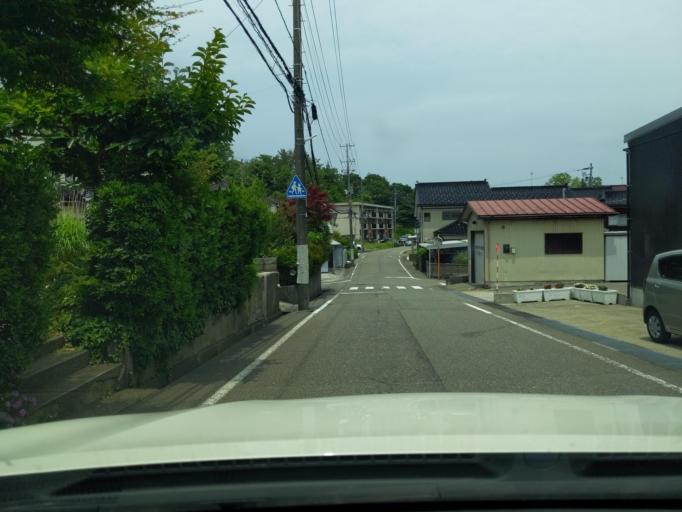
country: JP
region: Niigata
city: Kashiwazaki
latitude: 37.3549
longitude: 138.5409
